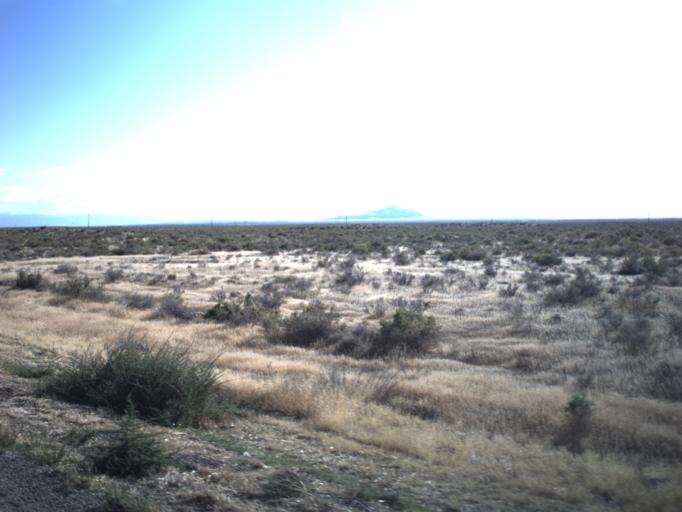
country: US
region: Utah
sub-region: Millard County
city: Delta
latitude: 39.3053
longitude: -112.4741
